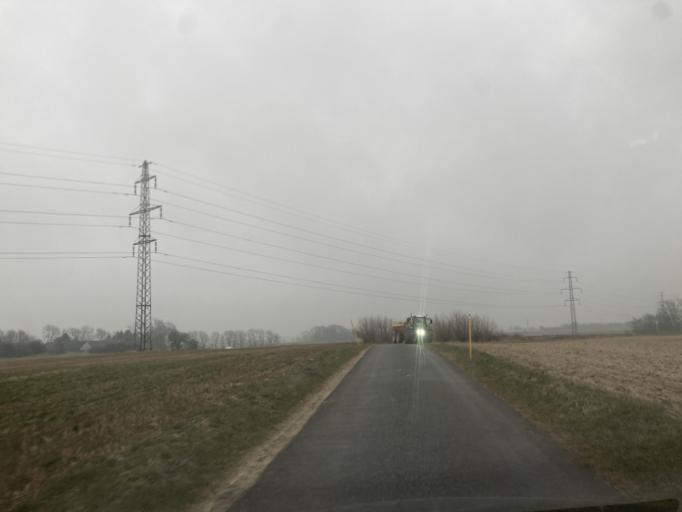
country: DK
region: Zealand
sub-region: Vordingborg Kommune
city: Neder Vindinge
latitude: 55.1562
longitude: 11.9011
